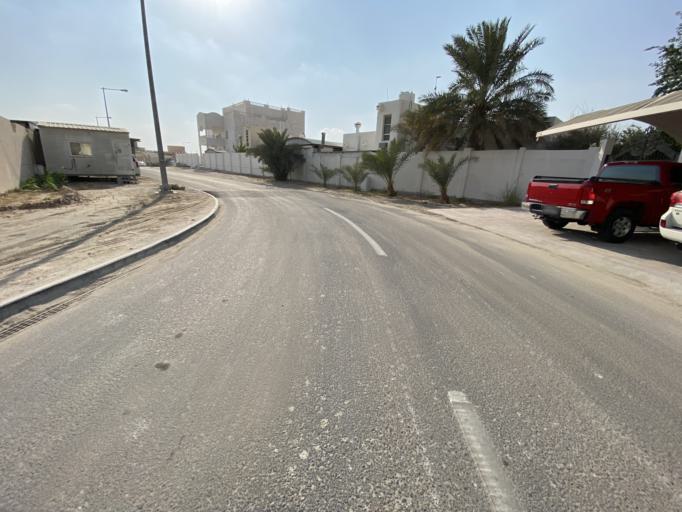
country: QA
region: Baladiyat ar Rayyan
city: Ar Rayyan
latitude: 25.2355
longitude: 51.3761
